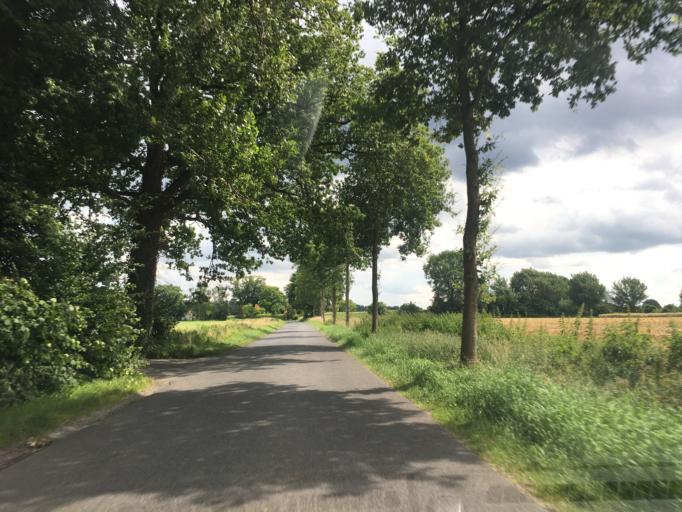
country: DE
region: North Rhine-Westphalia
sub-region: Regierungsbezirk Munster
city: Muenster
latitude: 51.9691
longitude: 7.6968
